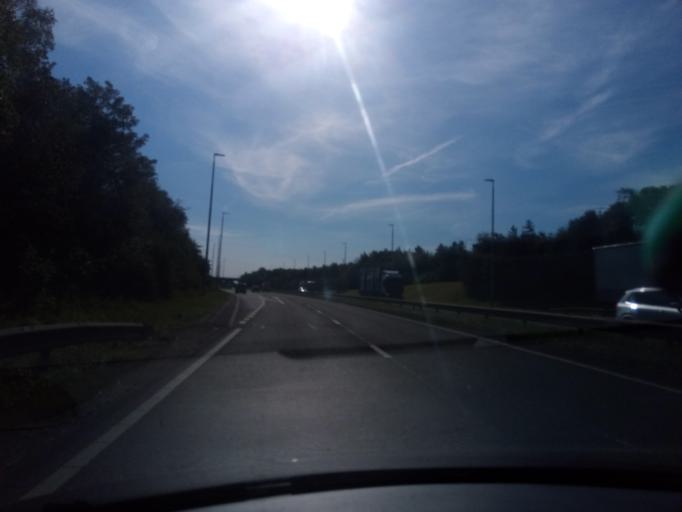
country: GB
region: England
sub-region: County Durham
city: Hawthorn
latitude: 54.8044
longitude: -1.3597
